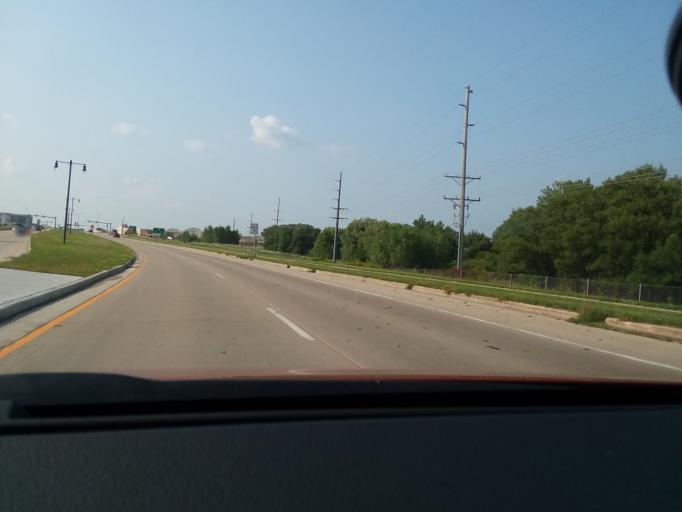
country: US
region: Wisconsin
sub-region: Dane County
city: Sun Prairie
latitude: 43.1575
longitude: -89.2653
